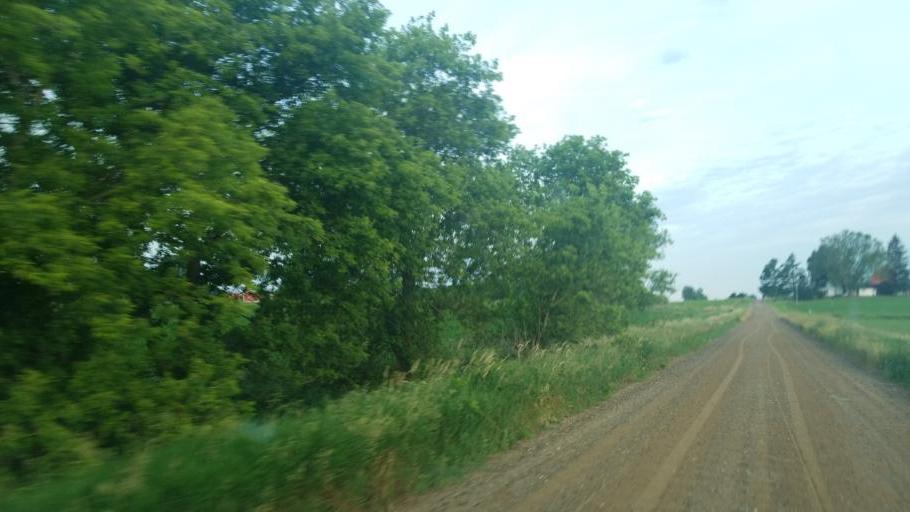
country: US
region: Michigan
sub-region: Eaton County
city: Charlotte
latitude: 42.5972
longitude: -84.9323
